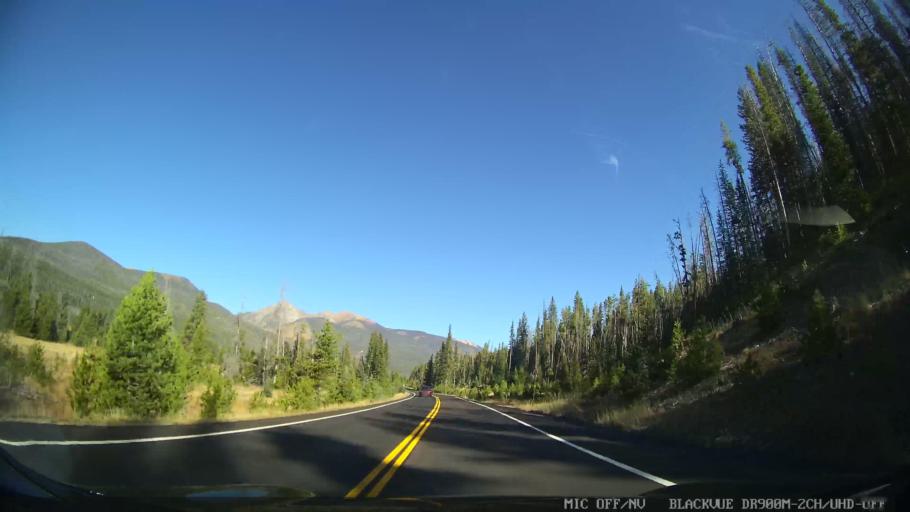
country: US
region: Colorado
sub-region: Grand County
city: Granby
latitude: 40.3334
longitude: -105.8550
